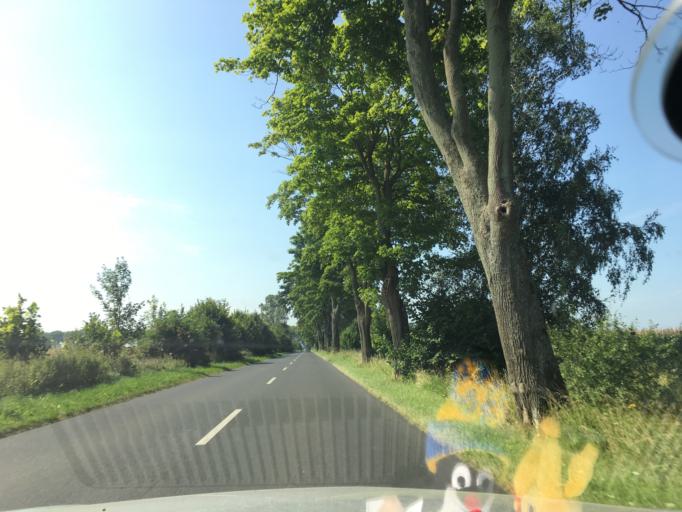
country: PL
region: West Pomeranian Voivodeship
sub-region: Powiat kamienski
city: Dziwnow
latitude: 54.0056
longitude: 14.8414
